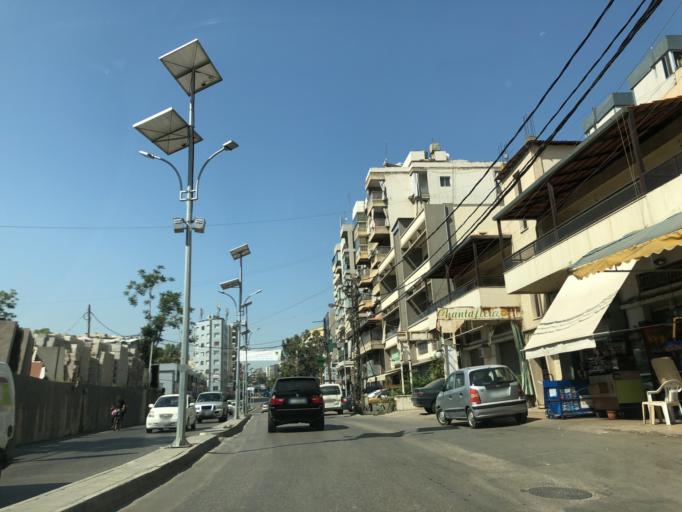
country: LB
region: Mont-Liban
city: Jdaidet el Matn
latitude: 33.8742
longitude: 35.5467
